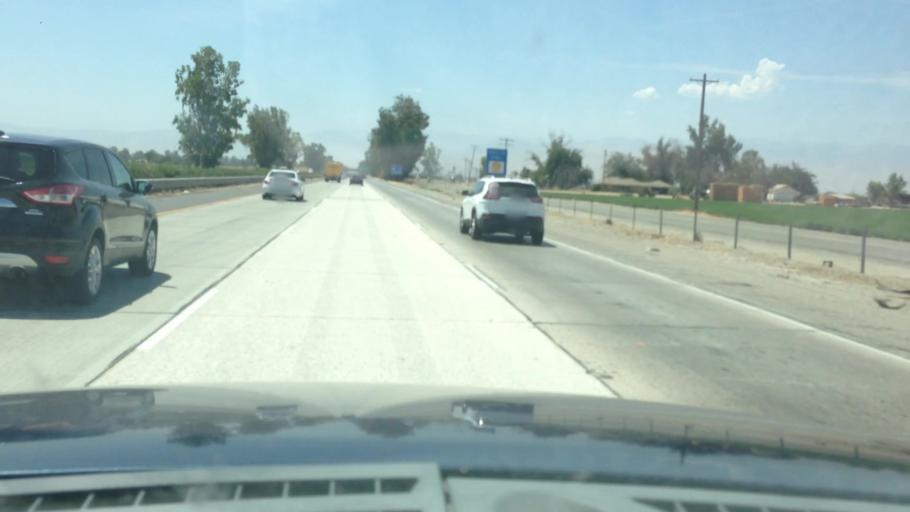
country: US
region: California
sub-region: Kern County
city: Greenfield
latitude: 35.2195
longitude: -119.0121
